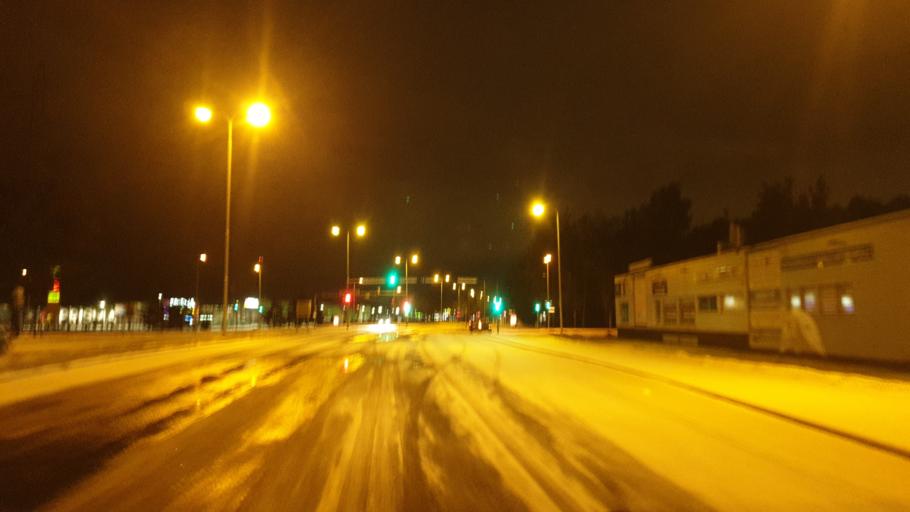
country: FI
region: Northern Ostrobothnia
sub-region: Oulu
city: Oulu
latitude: 64.9914
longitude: 25.4659
